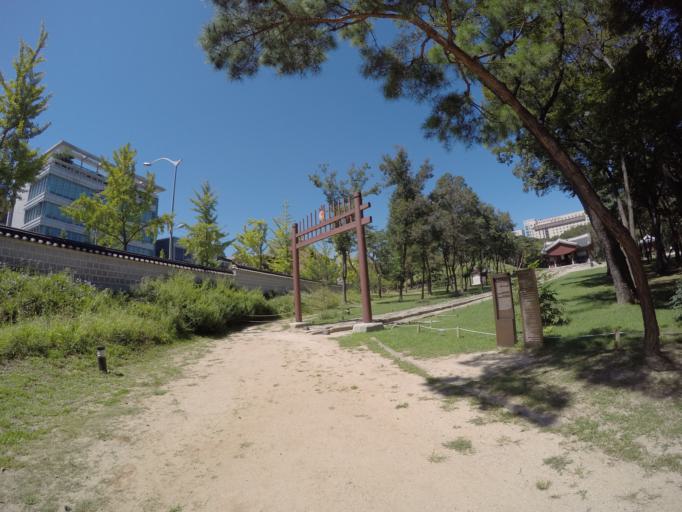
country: KR
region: Seoul
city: Seoul
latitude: 37.5074
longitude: 127.0467
